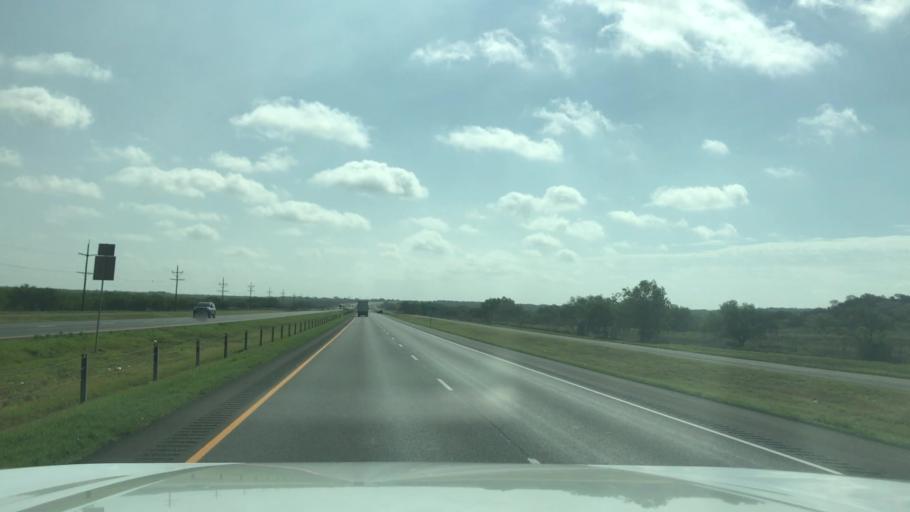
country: US
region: Texas
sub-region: Nolan County
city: Sweetwater
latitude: 32.4947
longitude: -100.2873
